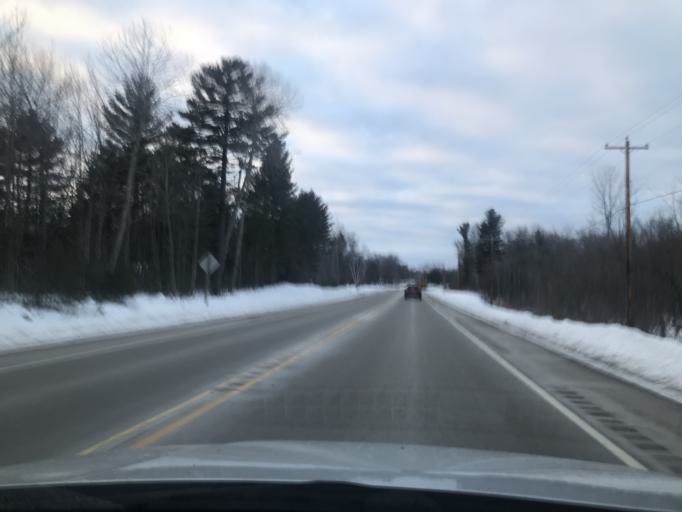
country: US
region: Wisconsin
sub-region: Marinette County
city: Marinette
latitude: 45.1601
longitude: -87.7209
